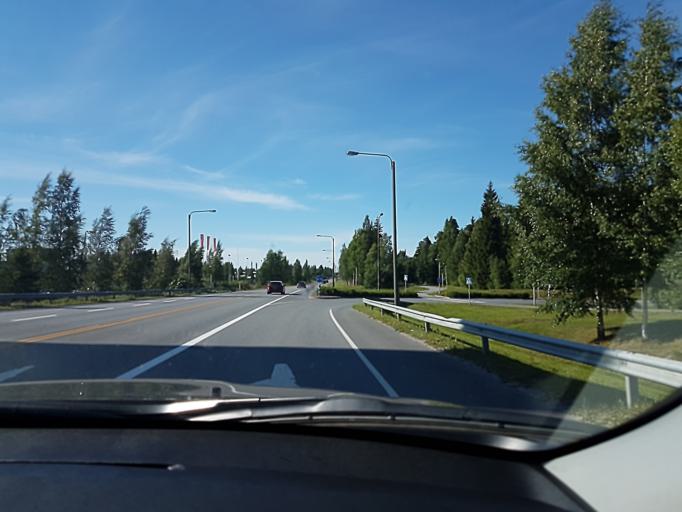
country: FI
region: Southern Ostrobothnia
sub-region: Seinaejoki
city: Nurmo
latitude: 62.7940
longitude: 22.8784
